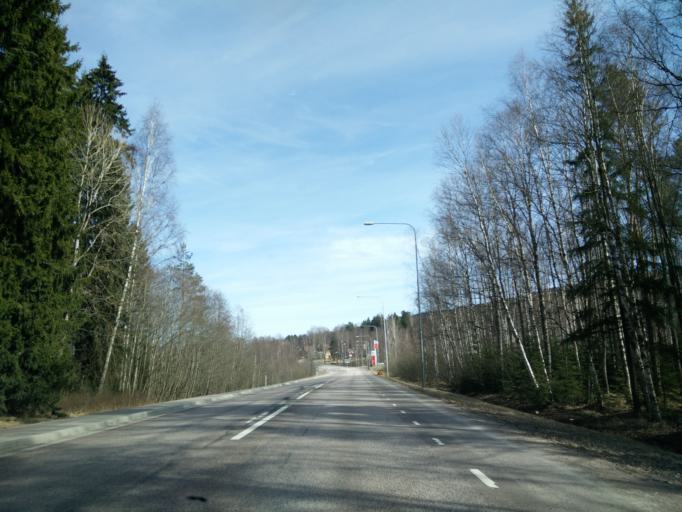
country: SE
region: Vaermland
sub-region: Hagfors Kommun
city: Hagfors
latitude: 60.0190
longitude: 13.6872
